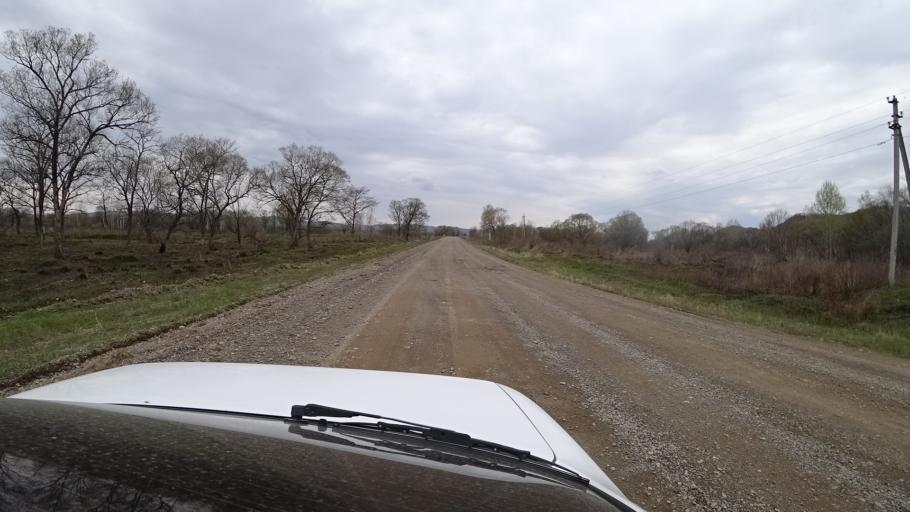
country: RU
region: Primorskiy
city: Novopokrovka
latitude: 45.5615
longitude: 134.3367
